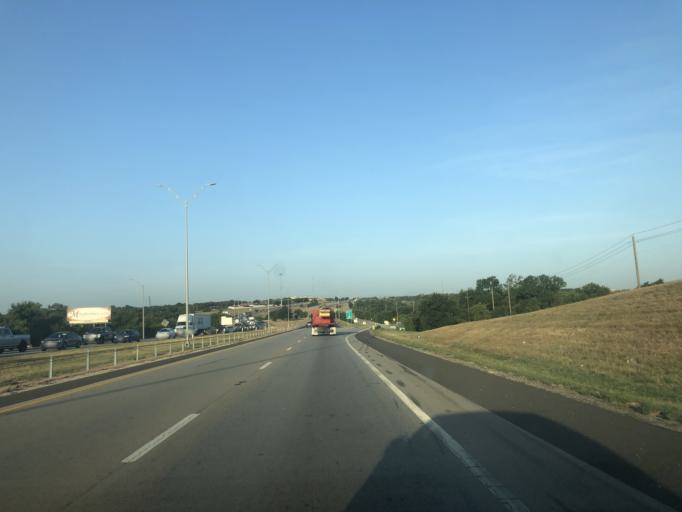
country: US
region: Texas
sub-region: Tarrant County
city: White Settlement
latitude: 32.7250
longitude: -97.5139
